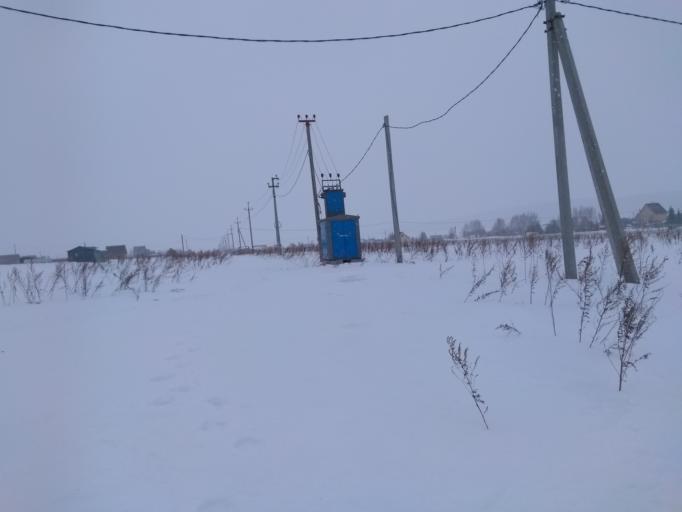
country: RU
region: Perm
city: Sylva
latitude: 57.8456
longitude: 56.7860
